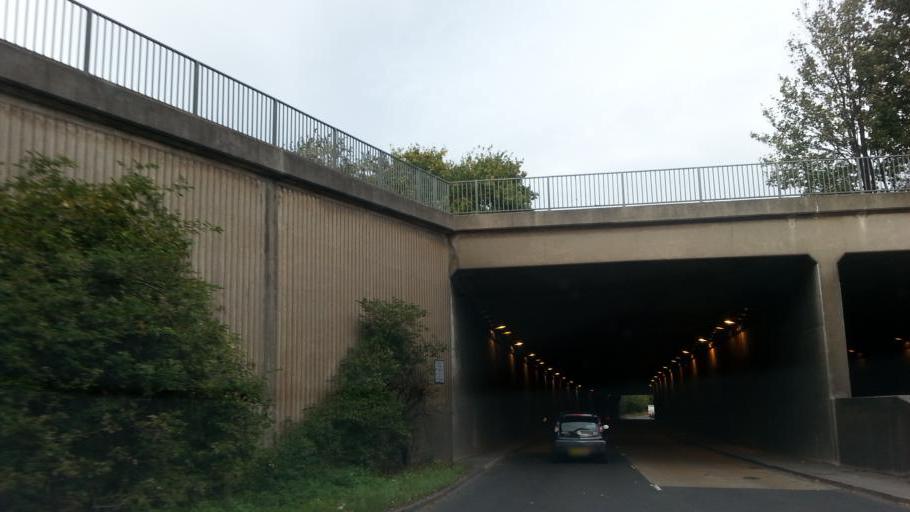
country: GB
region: England
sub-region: City and Borough of Leeds
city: Leeds
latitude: 53.7823
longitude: -1.5687
